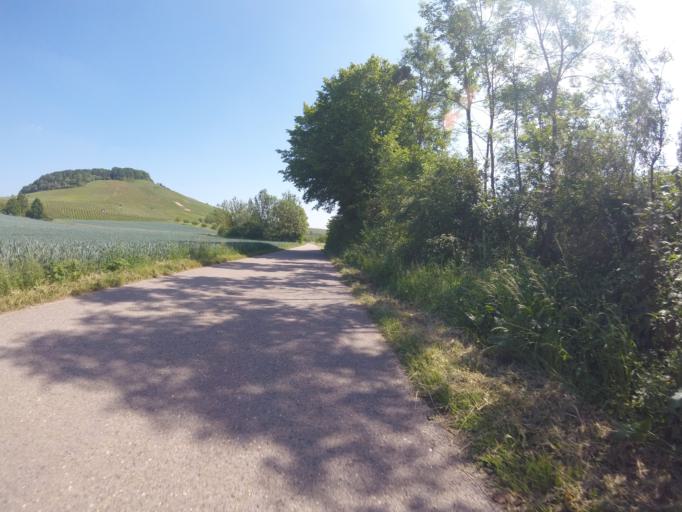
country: DE
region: Baden-Wuerttemberg
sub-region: Regierungsbezirk Stuttgart
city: Grossbottwar
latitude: 48.9922
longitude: 9.2900
